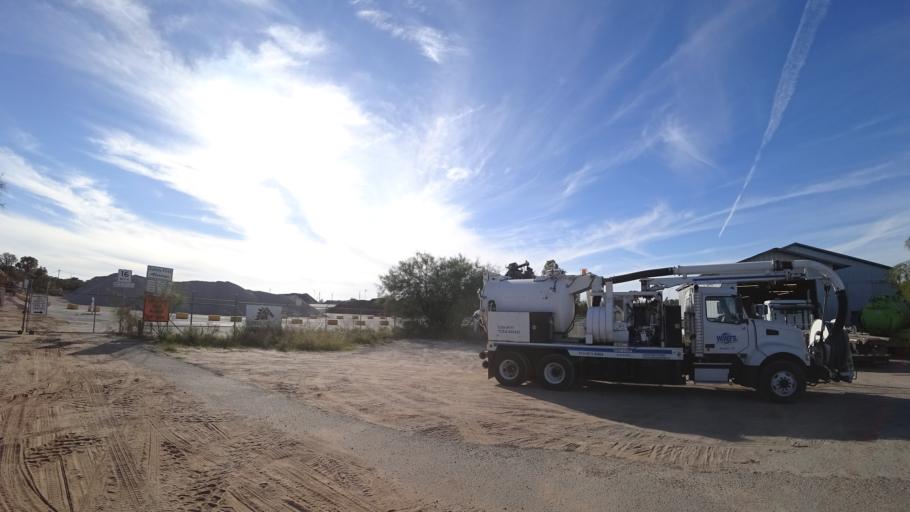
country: US
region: Texas
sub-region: Travis County
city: Austin
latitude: 30.2496
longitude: -97.6812
